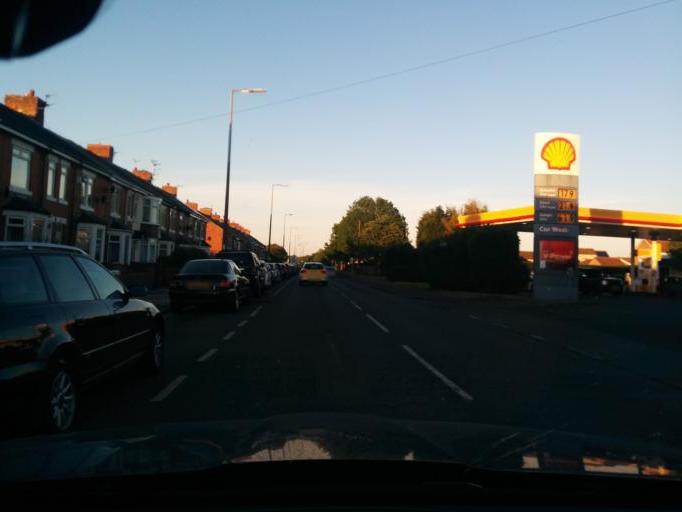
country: GB
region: England
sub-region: Northumberland
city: Ashington
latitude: 55.1703
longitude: -1.5569
